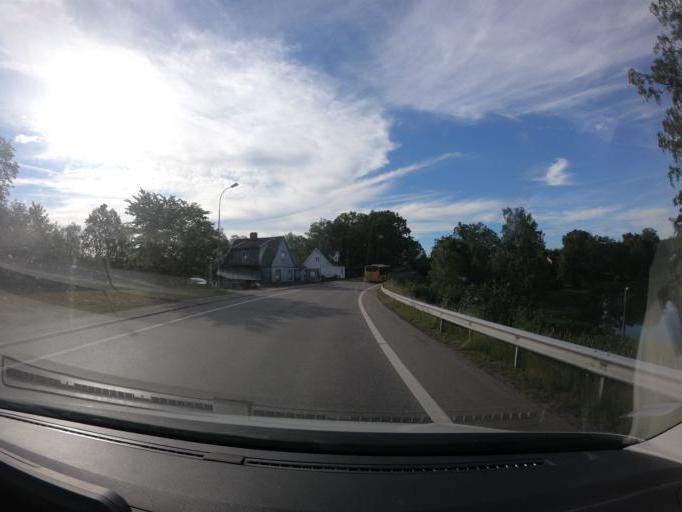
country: SE
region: Skane
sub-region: Orkelljunga Kommun
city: OErkelljunga
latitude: 56.2789
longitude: 13.2785
